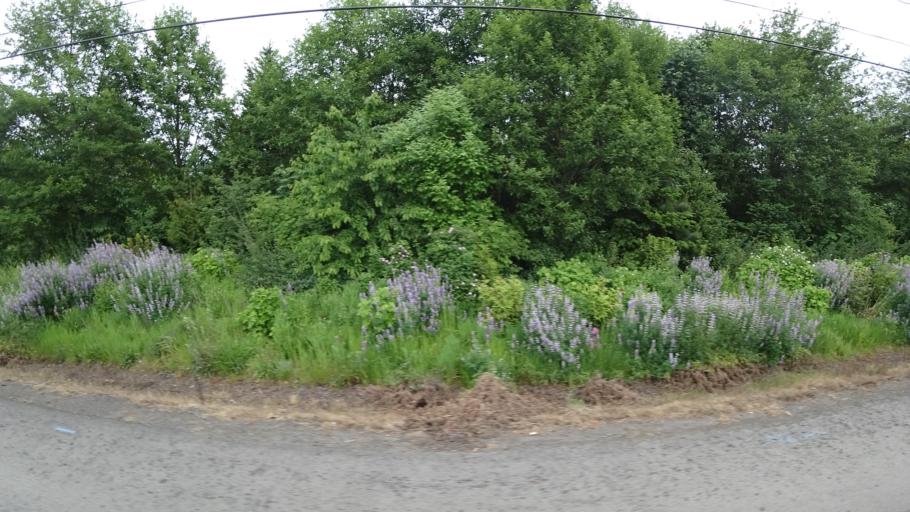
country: US
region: Oregon
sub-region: Washington County
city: Hillsboro
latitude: 45.5023
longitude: -122.9909
